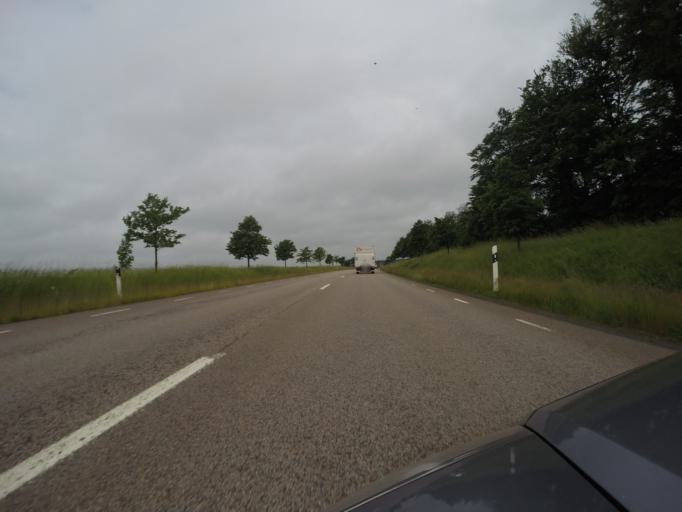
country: SE
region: Skane
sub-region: Bjuvs Kommun
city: Billesholm
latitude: 56.0113
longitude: 12.9386
